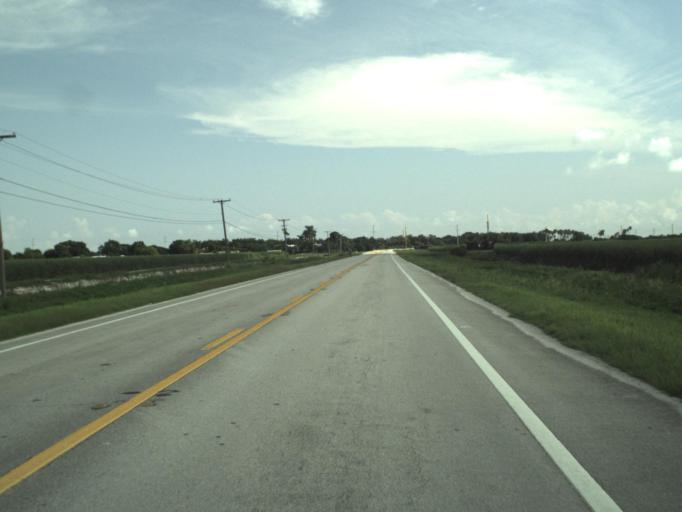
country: US
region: Florida
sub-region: Palm Beach County
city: Belle Glade
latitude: 26.7357
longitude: -80.6841
